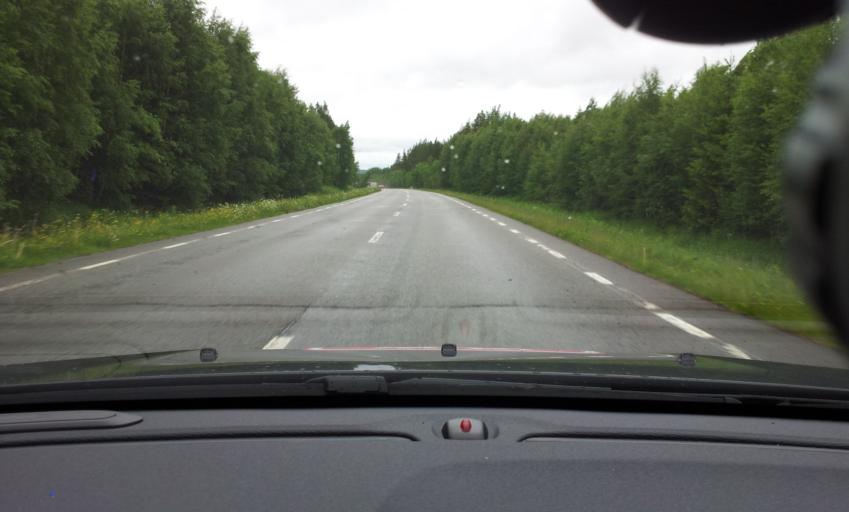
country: SE
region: Jaemtland
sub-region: OEstersunds Kommun
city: Lit
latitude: 63.6056
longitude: 14.6700
